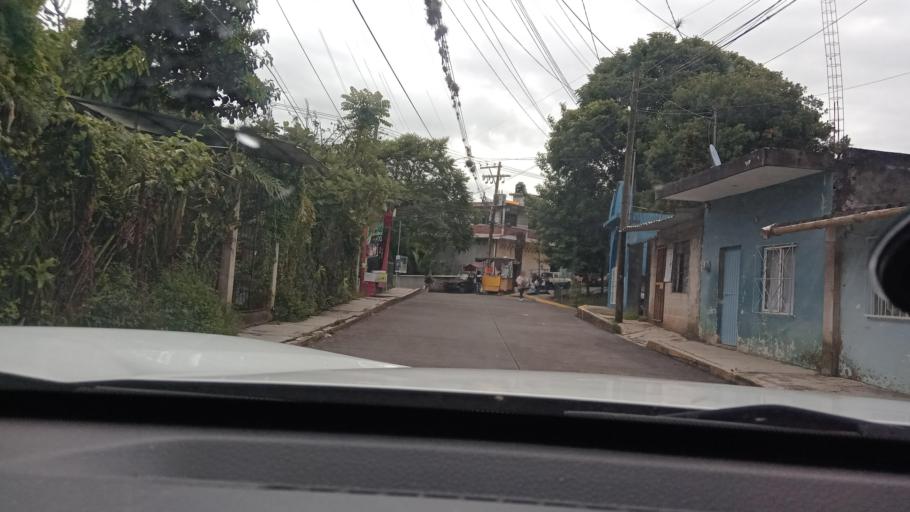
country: MX
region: Veracruz
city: Coatepec
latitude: 19.4480
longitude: -96.9616
